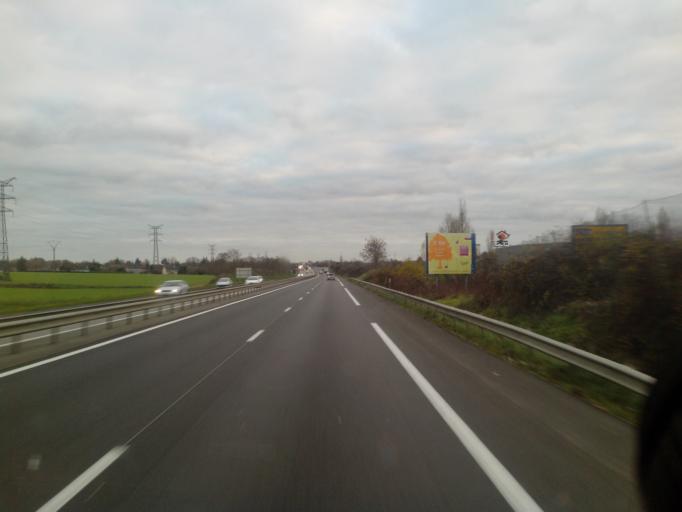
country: FR
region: Poitou-Charentes
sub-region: Departement de la Vienne
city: Montamise
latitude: 46.5912
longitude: 0.3918
